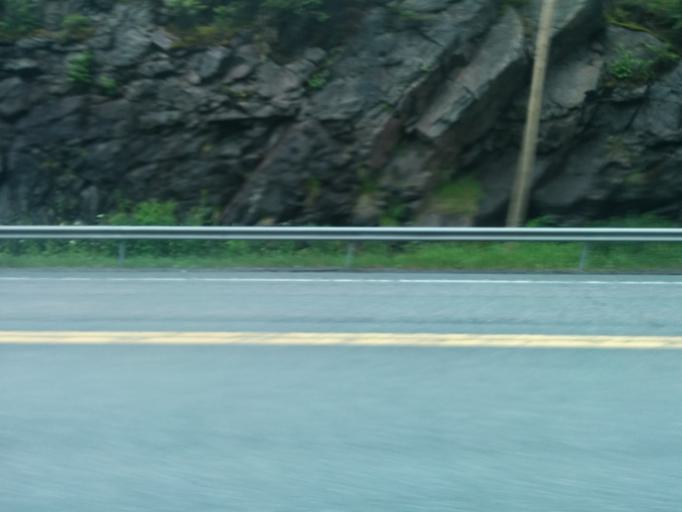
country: FI
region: Pirkanmaa
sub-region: Tampere
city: Orivesi
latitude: 61.6846
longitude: 24.3496
